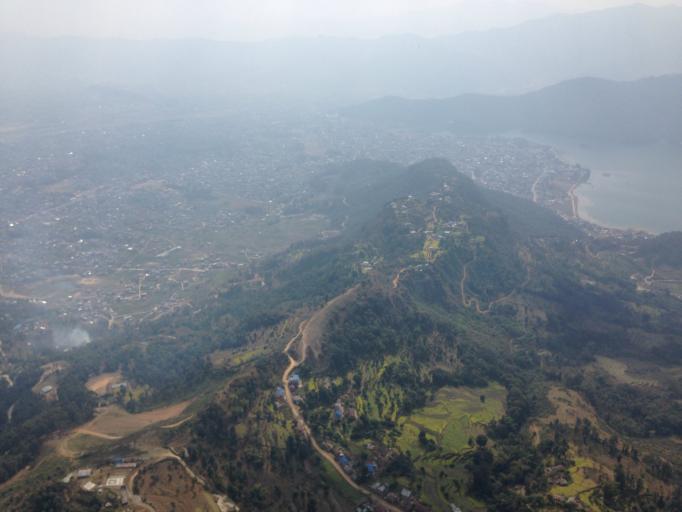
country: NP
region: Western Region
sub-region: Gandaki Zone
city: Pokhara
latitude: 28.2409
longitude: 83.9655
